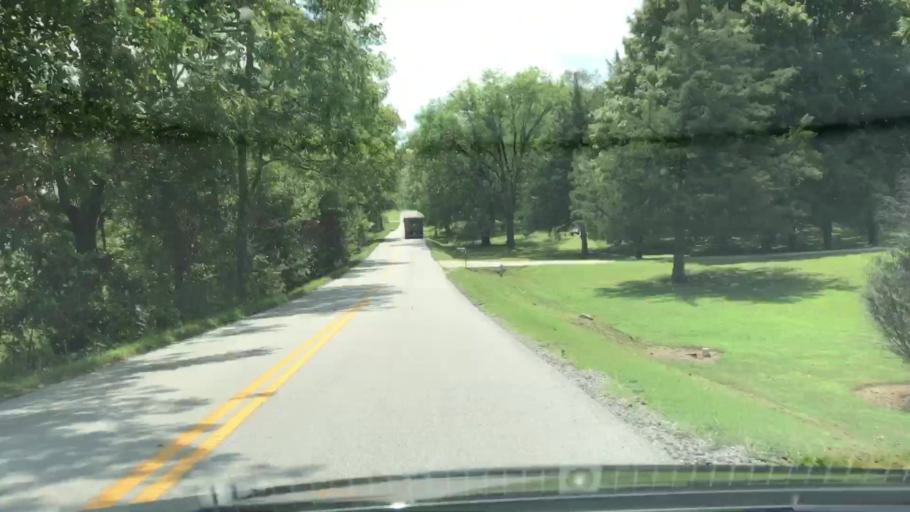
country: US
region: Tennessee
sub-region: Robertson County
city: Springfield
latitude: 36.6473
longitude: -86.9822
